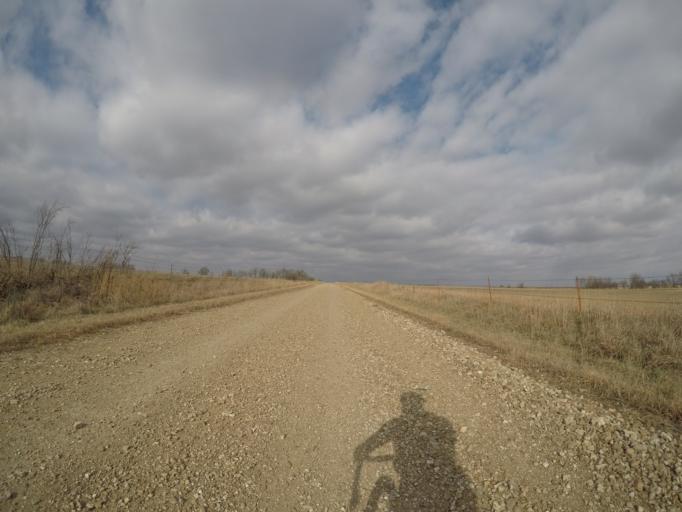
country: US
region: Kansas
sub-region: Morris County
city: Council Grove
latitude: 38.7875
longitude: -96.3527
